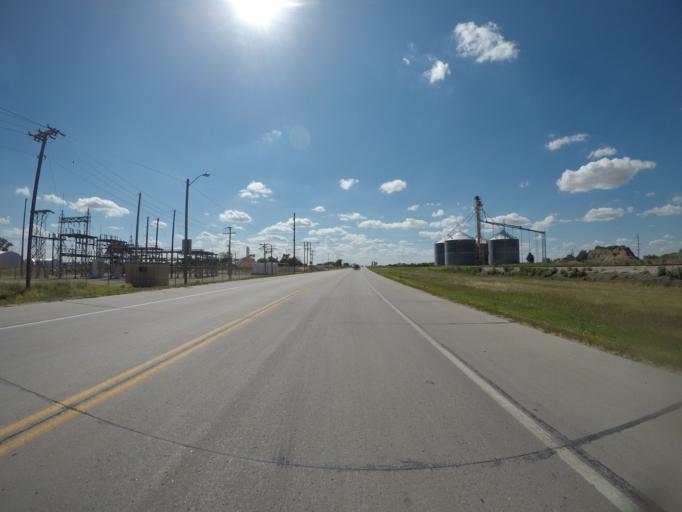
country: US
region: Colorado
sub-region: Phillips County
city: Holyoke
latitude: 40.5852
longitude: -102.3108
